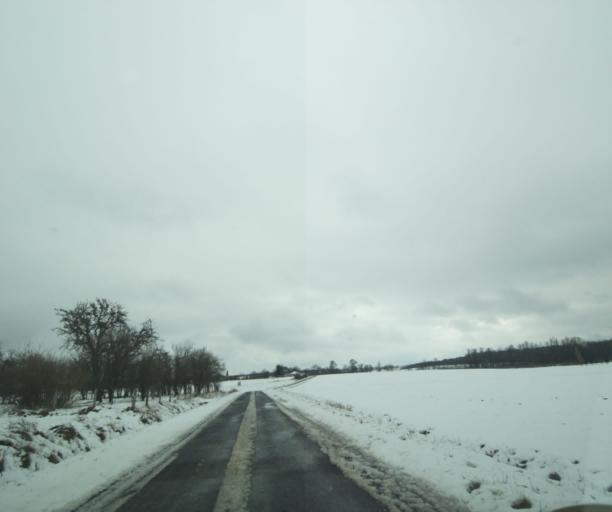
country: FR
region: Champagne-Ardenne
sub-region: Departement de la Haute-Marne
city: Montier-en-Der
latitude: 48.4175
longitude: 4.7334
